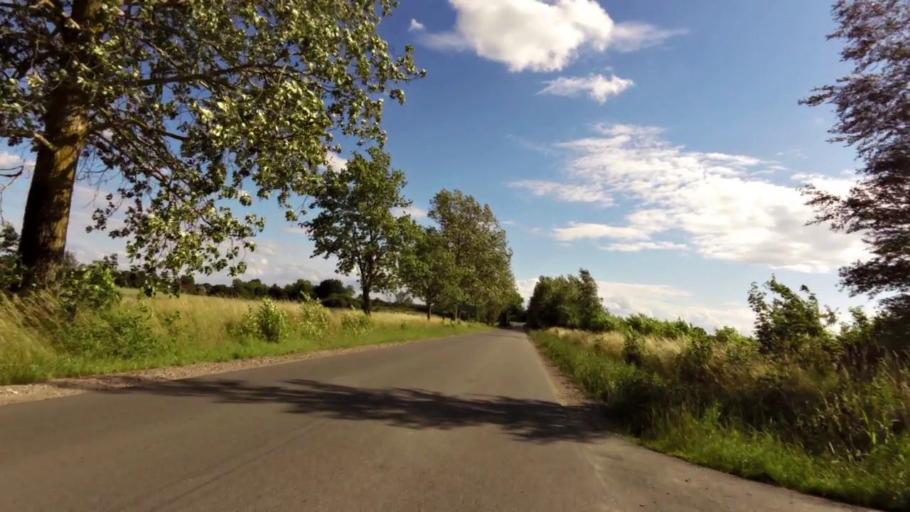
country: PL
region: West Pomeranian Voivodeship
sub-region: Powiat slawienski
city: Slawno
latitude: 54.4400
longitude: 16.7336
